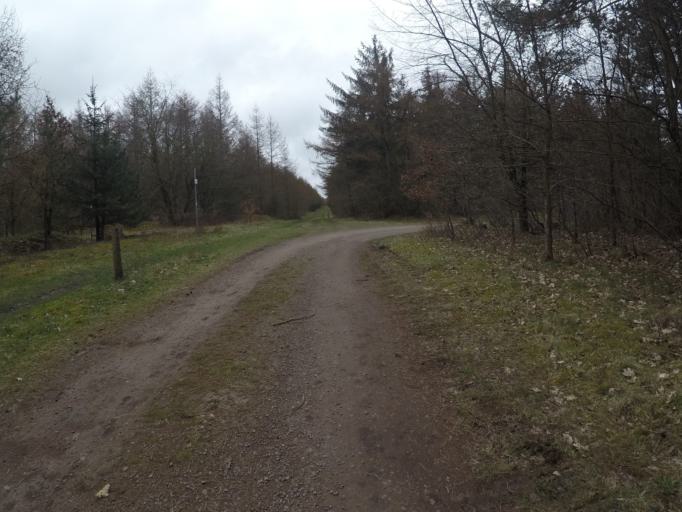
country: DE
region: Lower Saxony
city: Nordholz
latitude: 53.8243
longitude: 8.6039
